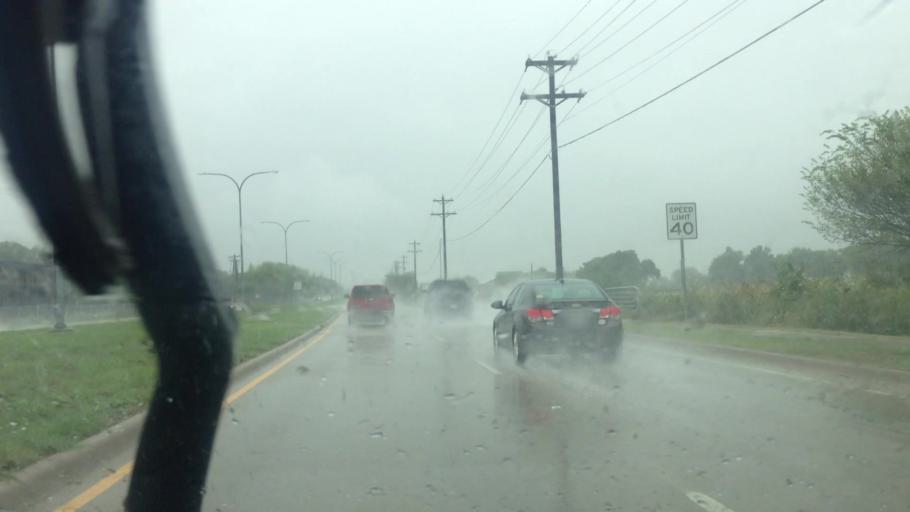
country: US
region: Texas
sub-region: Tarrant County
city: Keller
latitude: 32.9317
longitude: -97.2907
